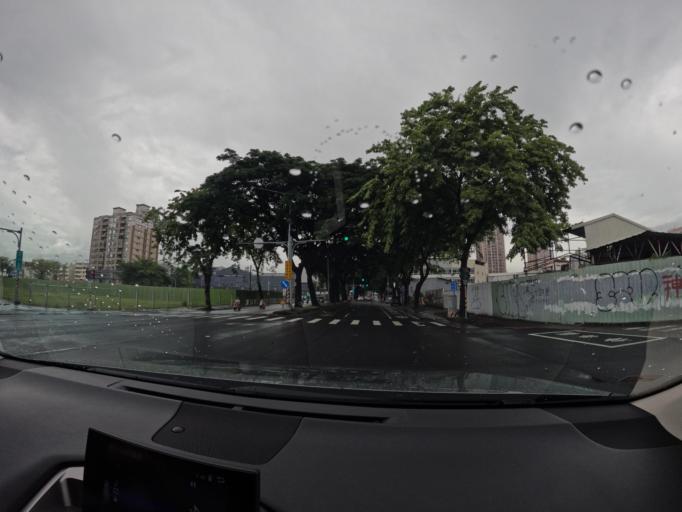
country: TW
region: Kaohsiung
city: Kaohsiung
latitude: 22.6559
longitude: 120.3126
